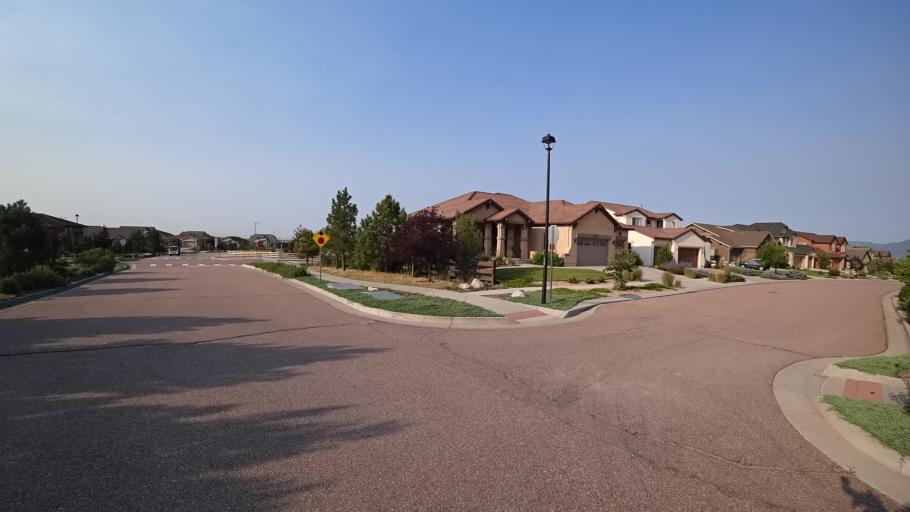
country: US
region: Colorado
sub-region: El Paso County
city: Black Forest
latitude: 38.9757
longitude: -104.7316
